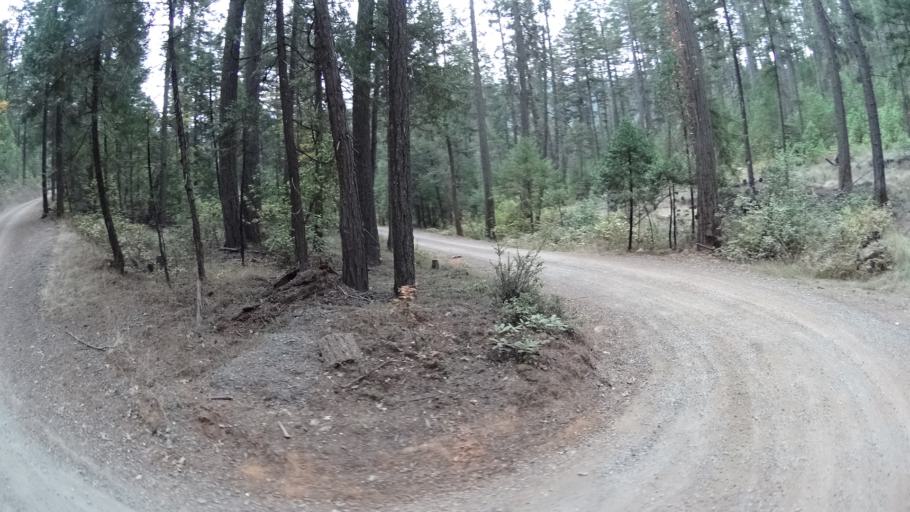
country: US
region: California
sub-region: Siskiyou County
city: Happy Camp
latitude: 41.7822
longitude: -123.3315
